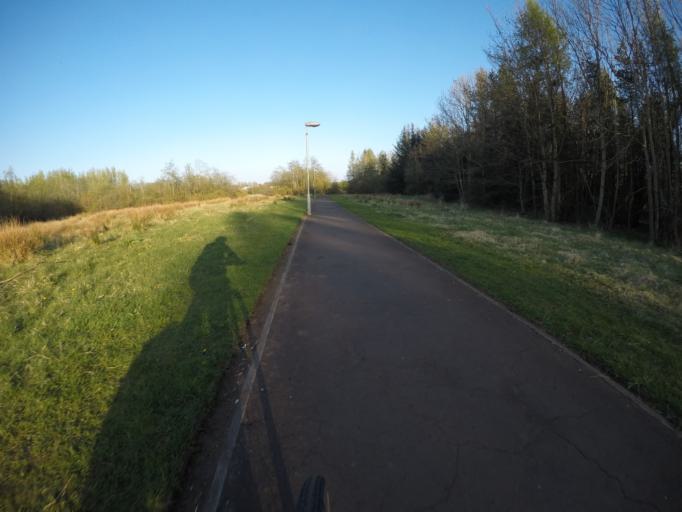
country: GB
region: Scotland
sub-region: North Ayrshire
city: Kilwinning
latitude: 55.6474
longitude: -4.6949
